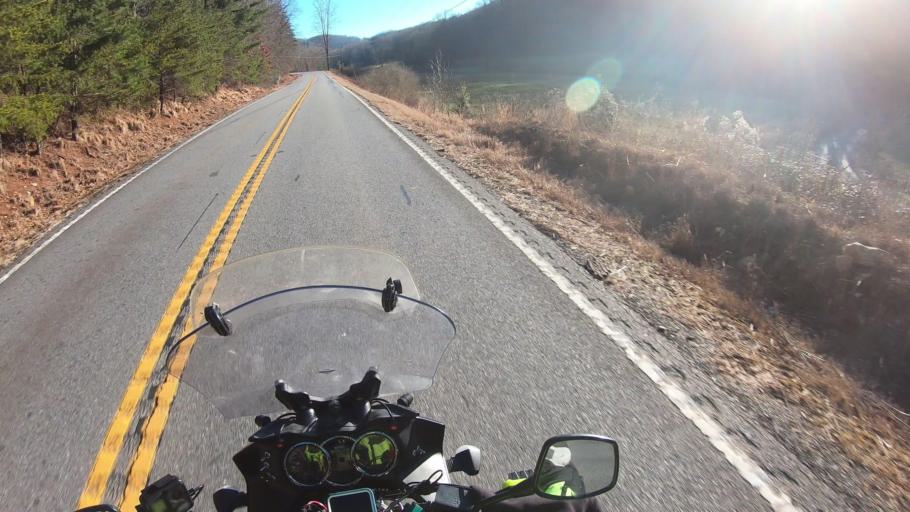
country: US
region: Georgia
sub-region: Fannin County
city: Blue Ridge
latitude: 34.8273
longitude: -84.1901
